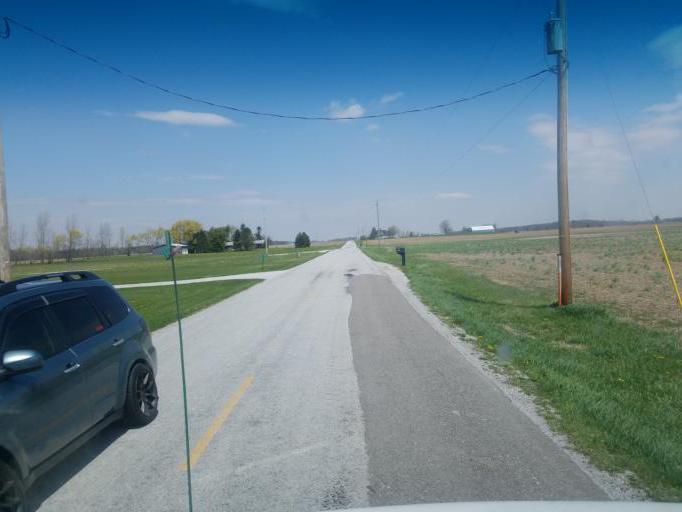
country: US
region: Ohio
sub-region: Hardin County
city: Forest
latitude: 40.7108
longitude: -83.5379
